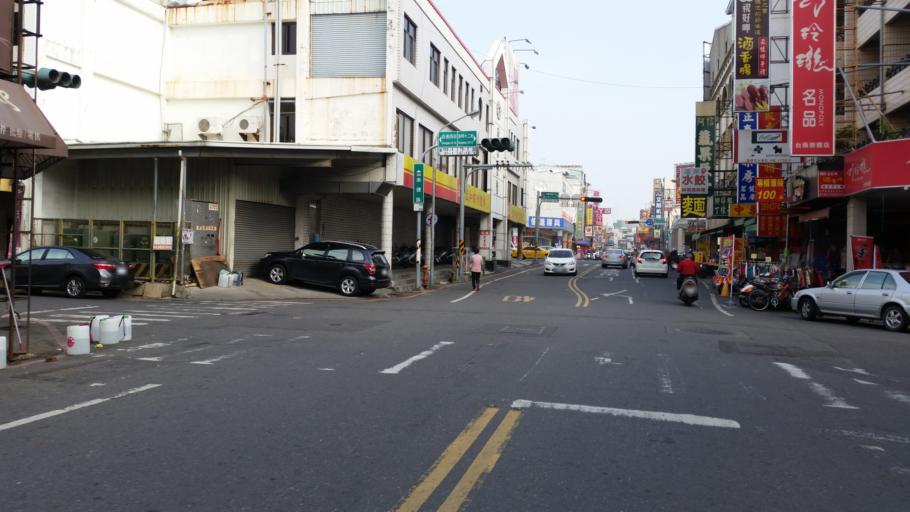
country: TW
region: Taiwan
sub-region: Tainan
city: Tainan
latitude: 22.9763
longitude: 120.2241
